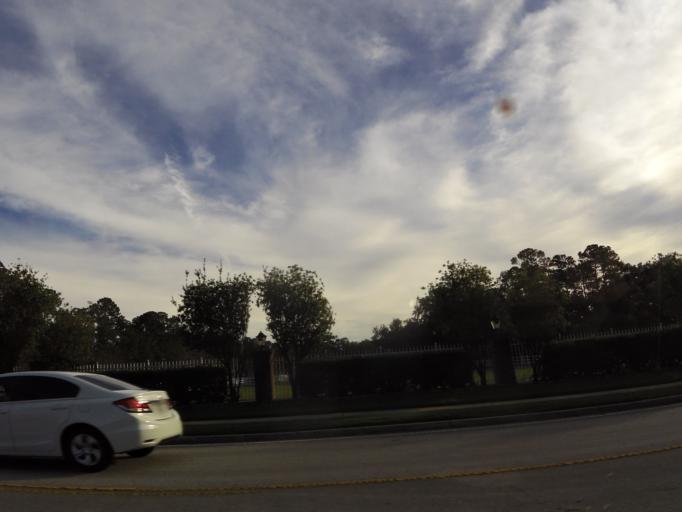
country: US
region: Florida
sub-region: Saint Johns County
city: Fruit Cove
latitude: 30.1616
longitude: -81.5669
